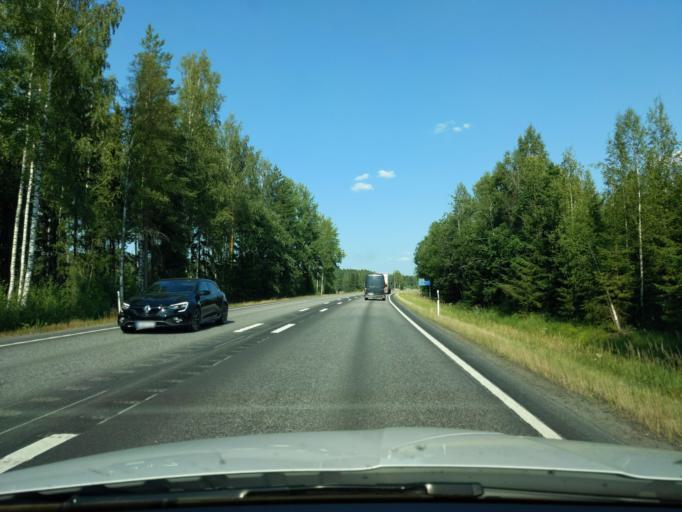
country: FI
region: Paijanne Tavastia
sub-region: Lahti
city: Jaervelae
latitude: 60.9082
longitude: 25.3311
